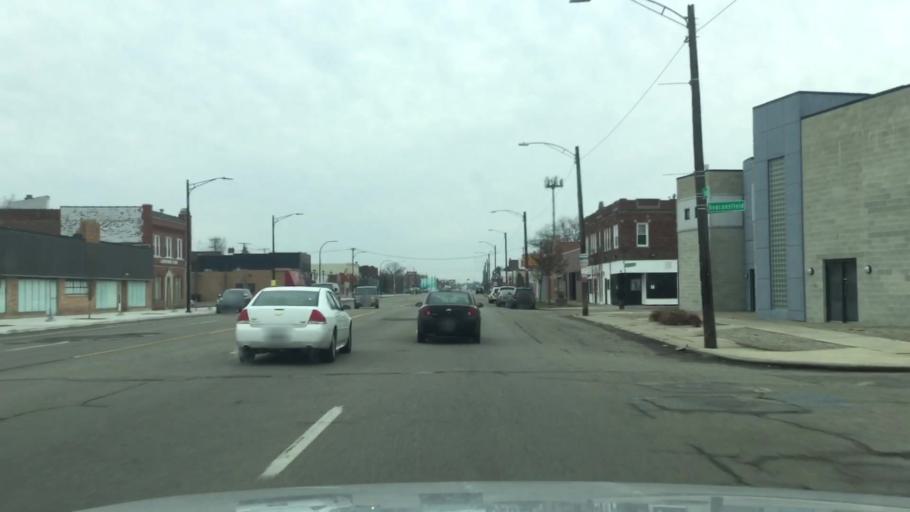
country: US
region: Michigan
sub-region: Wayne County
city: Grosse Pointe Park
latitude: 42.3882
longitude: -82.9427
